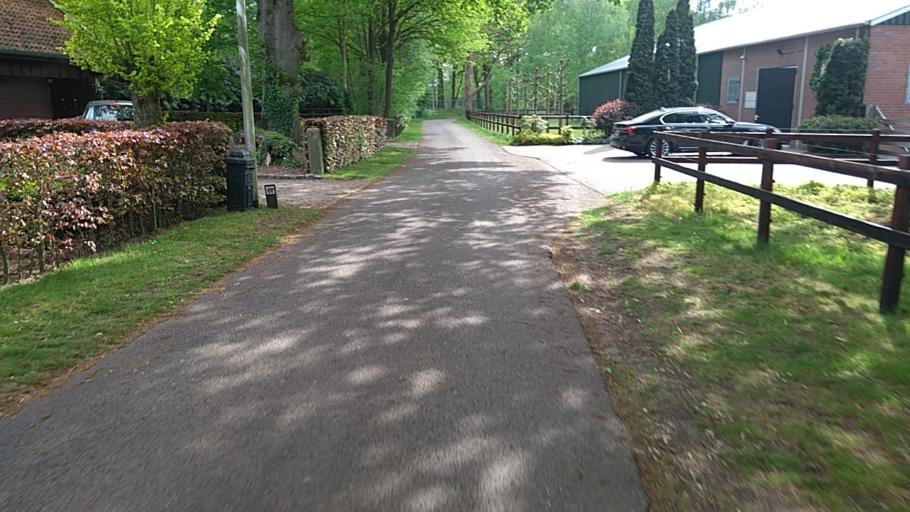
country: NL
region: Overijssel
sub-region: Gemeente Almelo
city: Almelo
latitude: 52.3714
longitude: 6.7100
